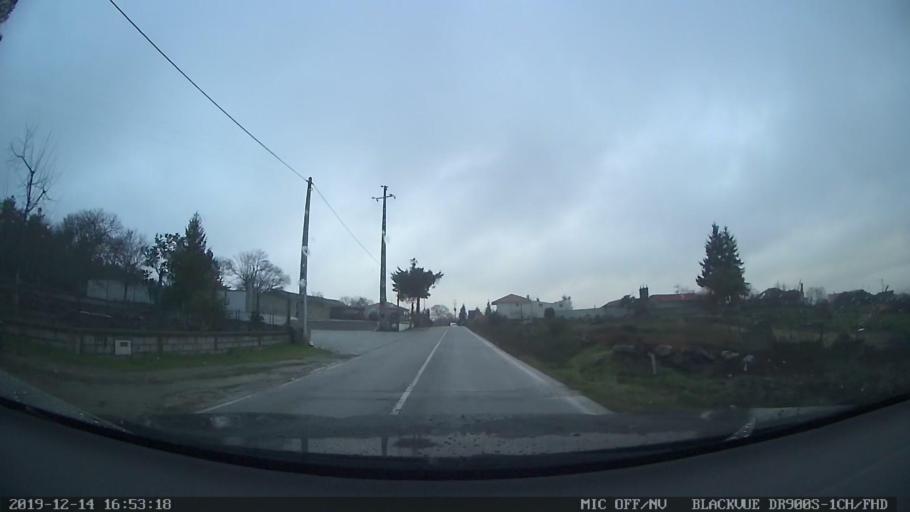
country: PT
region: Vila Real
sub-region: Murca
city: Murca
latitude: 41.4297
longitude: -7.5166
